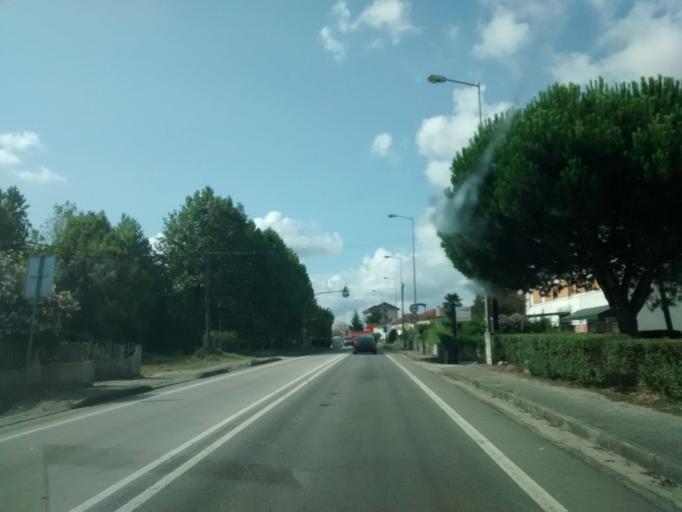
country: PT
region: Aveiro
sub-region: Mealhada
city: Mealhada
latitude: 40.3866
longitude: -8.4506
